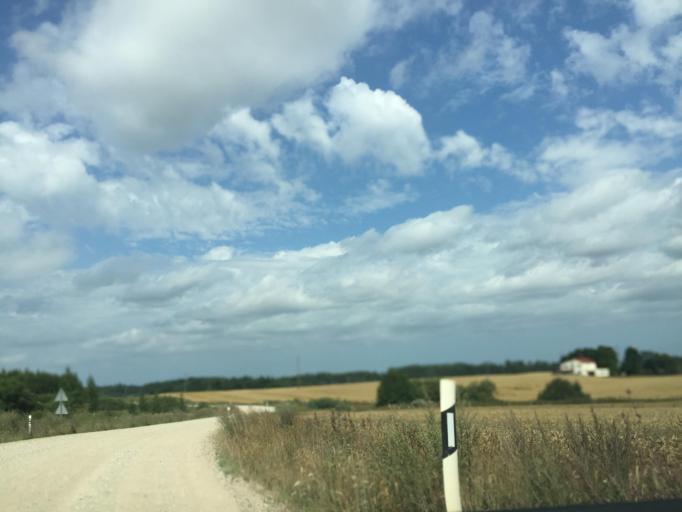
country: LV
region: Kandava
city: Kandava
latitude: 56.9983
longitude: 22.8670
